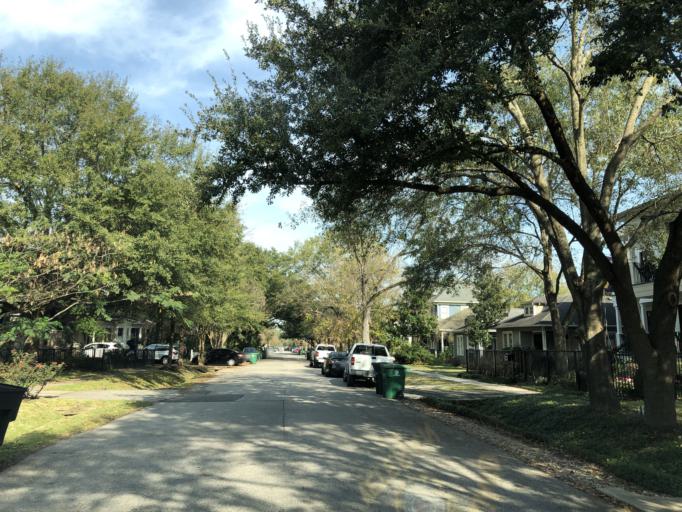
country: US
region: Texas
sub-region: Harris County
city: Houston
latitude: 29.7929
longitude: -95.3943
